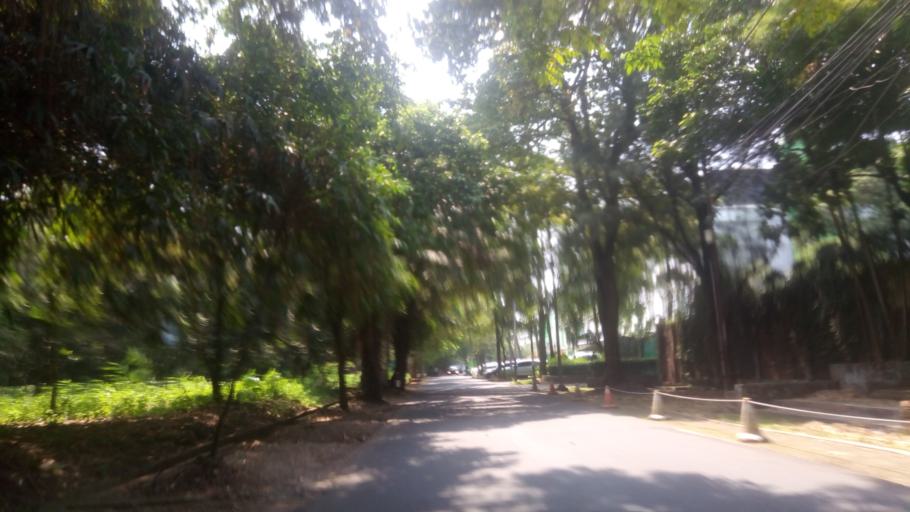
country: ID
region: Jakarta Raya
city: Jakarta
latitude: -6.2392
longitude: 106.8351
